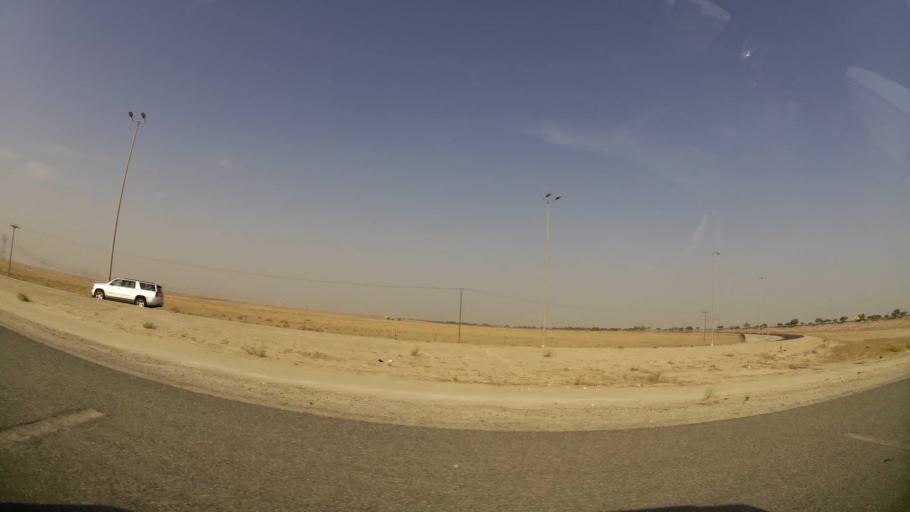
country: KW
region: Al Farwaniyah
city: Janub as Surrah
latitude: 29.1768
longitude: 47.9897
